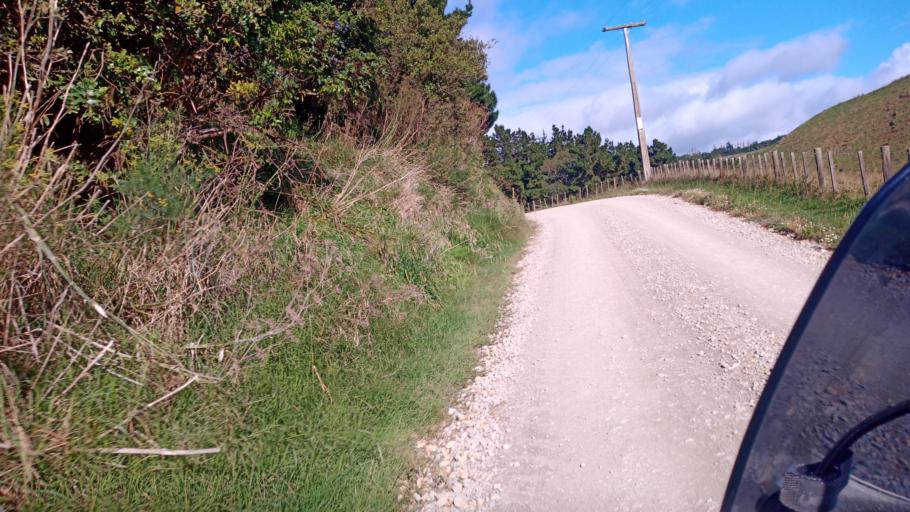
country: NZ
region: Gisborne
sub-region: Gisborne District
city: Gisborne
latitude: -38.5408
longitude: 177.5102
